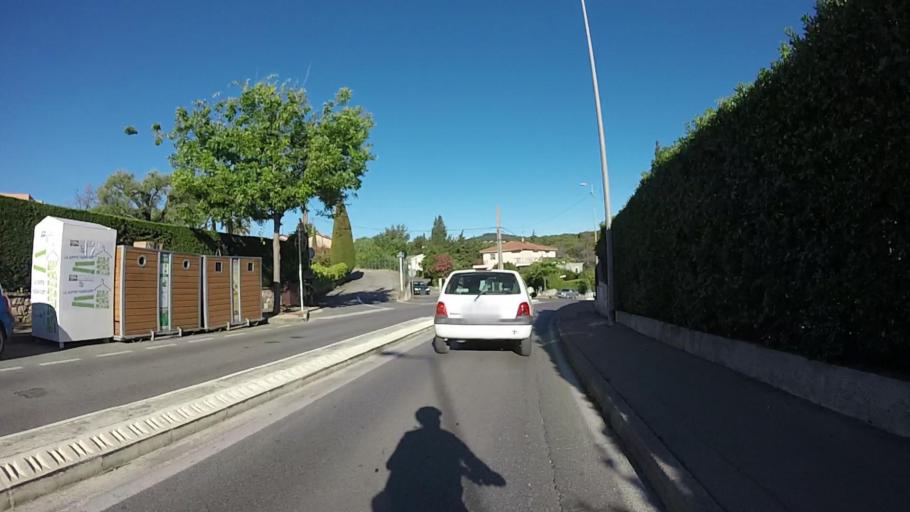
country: FR
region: Provence-Alpes-Cote d'Azur
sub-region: Departement des Alpes-Maritimes
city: Antibes
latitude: 43.5852
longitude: 7.0954
